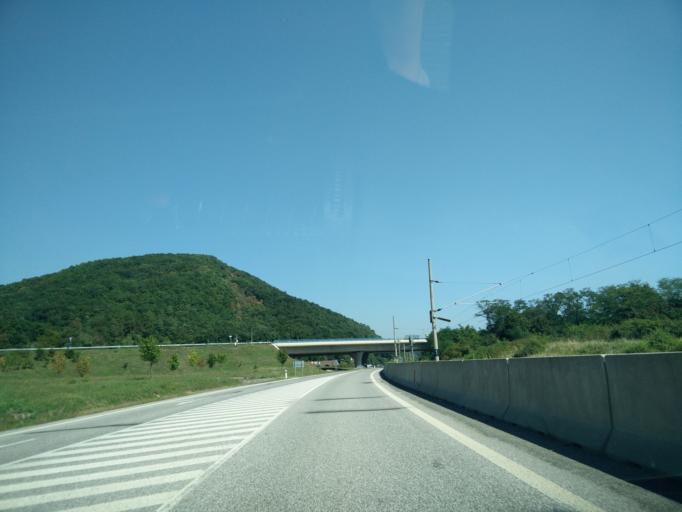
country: SK
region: Nitriansky
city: Tlmace
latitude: 48.3607
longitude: 18.5752
